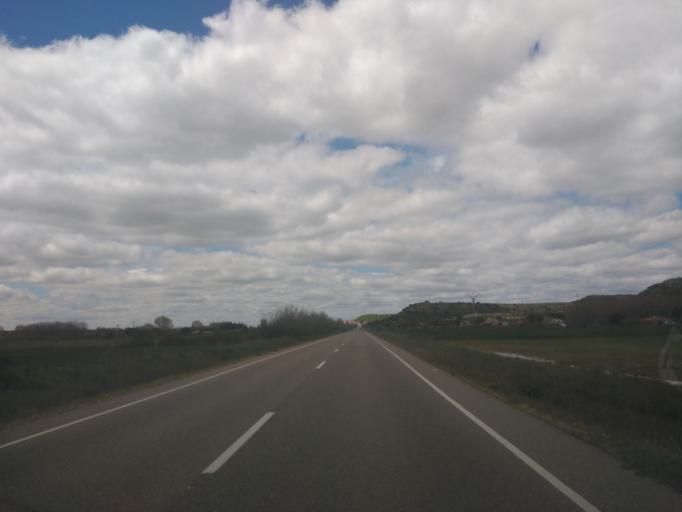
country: ES
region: Castille and Leon
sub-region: Provincia de Salamanca
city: Almenara de Tormes
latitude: 41.0554
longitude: -5.7988
